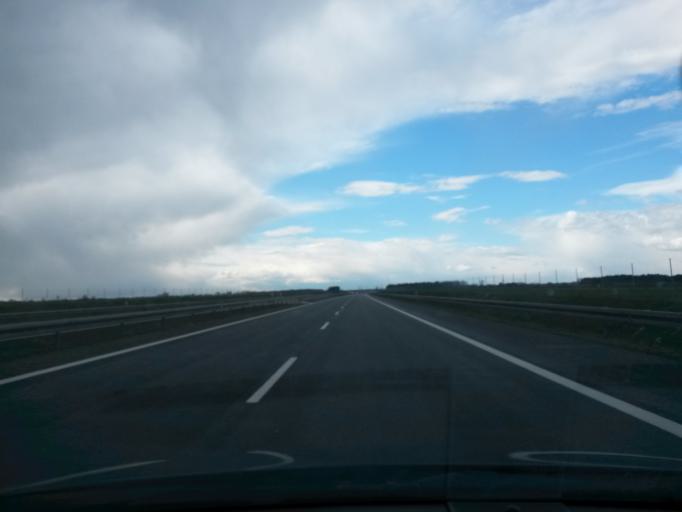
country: PL
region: Greater Poland Voivodeship
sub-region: Powiat slupecki
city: Ladek
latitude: 52.2155
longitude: 17.9744
